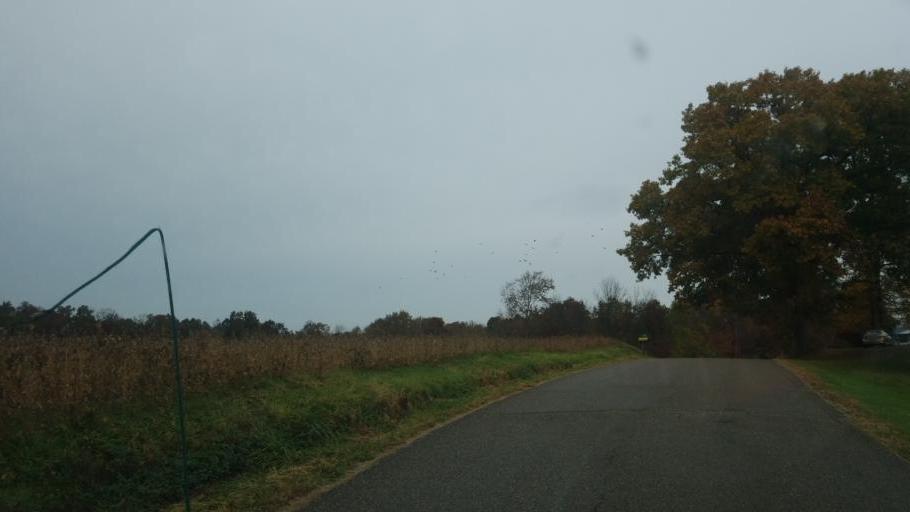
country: US
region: Ohio
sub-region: Washington County
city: Beverly
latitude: 39.5517
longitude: -81.7041
